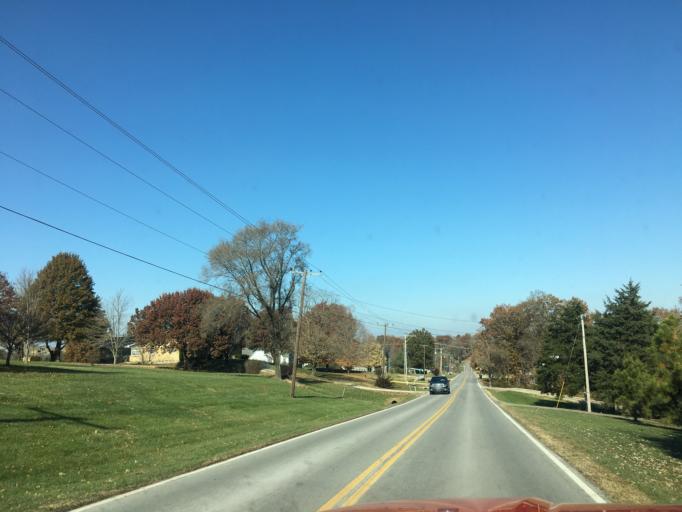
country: US
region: Missouri
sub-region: Cole County
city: Wardsville
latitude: 38.5106
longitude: -92.1759
